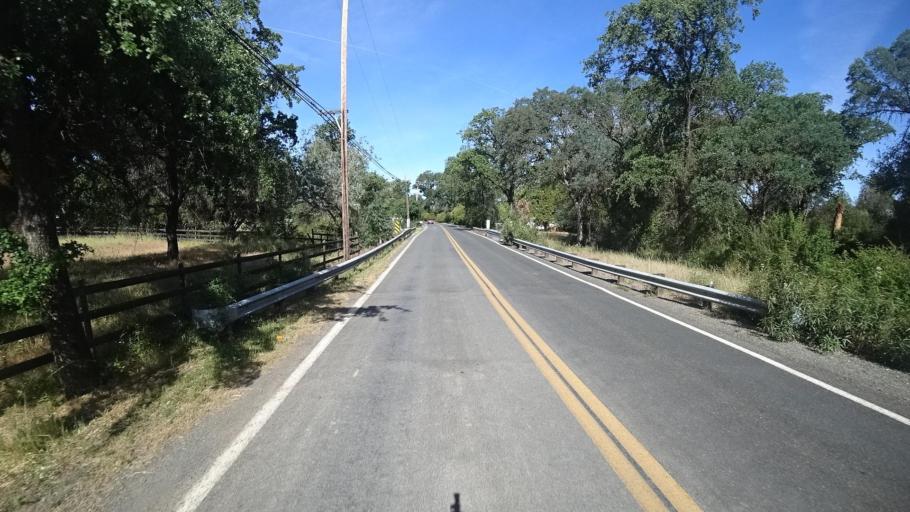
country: US
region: California
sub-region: Lake County
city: Kelseyville
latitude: 38.9715
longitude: -122.8597
